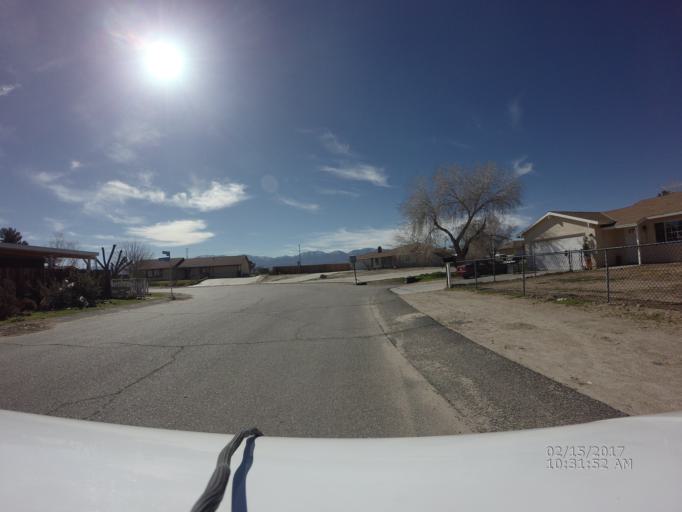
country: US
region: California
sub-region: Los Angeles County
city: Lake Los Angeles
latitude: 34.5816
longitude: -117.8605
